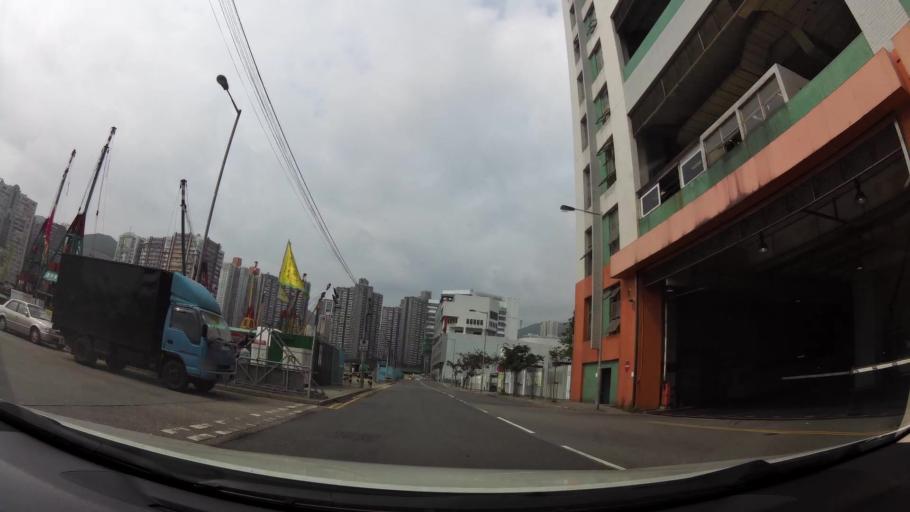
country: HK
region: Wanchai
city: Wan Chai
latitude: 22.2718
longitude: 114.2431
